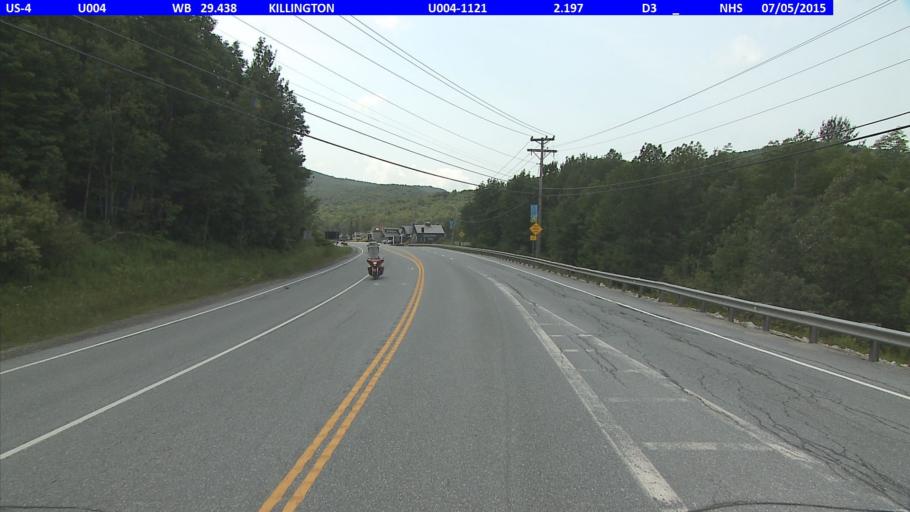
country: US
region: Vermont
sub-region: Rutland County
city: Rutland
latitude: 43.6680
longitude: -72.8066
